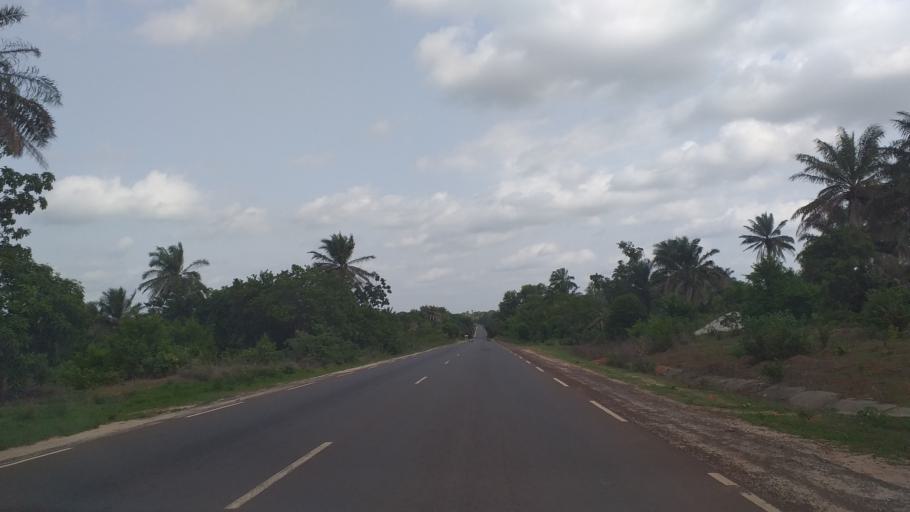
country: GN
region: Boke
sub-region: Boke Prefecture
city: Sangueya
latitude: 10.7400
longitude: -14.3791
